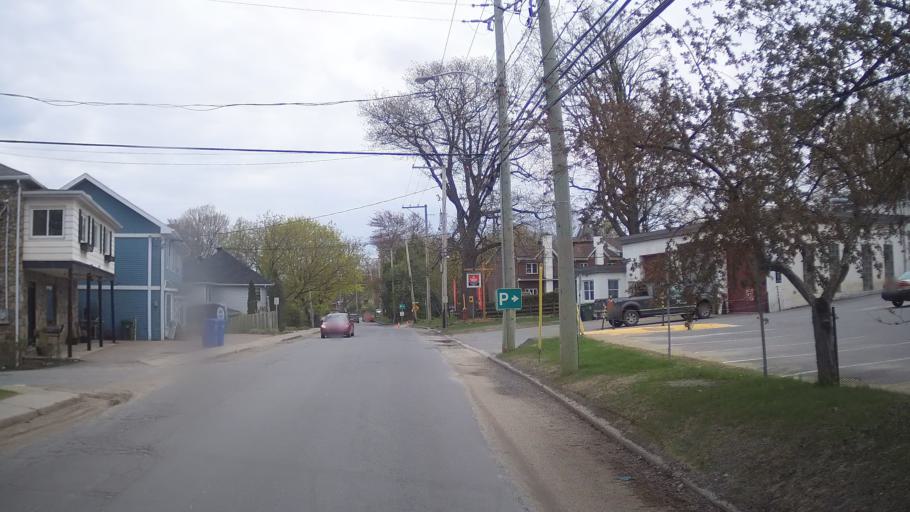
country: CA
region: Quebec
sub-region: Monteregie
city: Hudson
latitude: 45.4610
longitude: -74.1459
